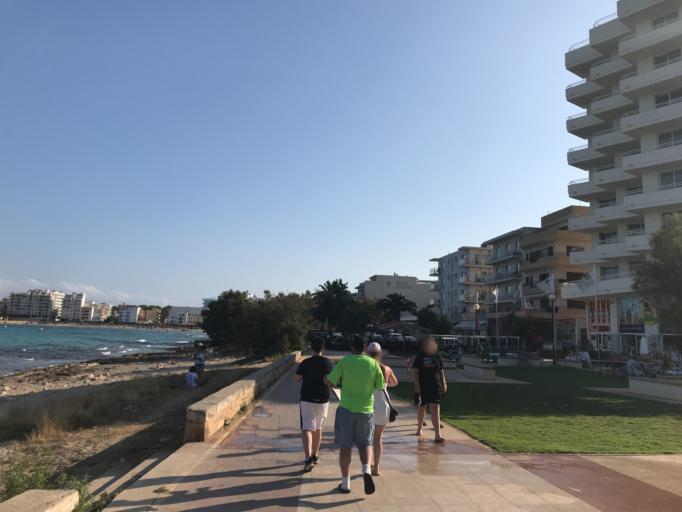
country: ES
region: Balearic Islands
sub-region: Illes Balears
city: Son Servera
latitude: 39.5694
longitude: 3.3747
